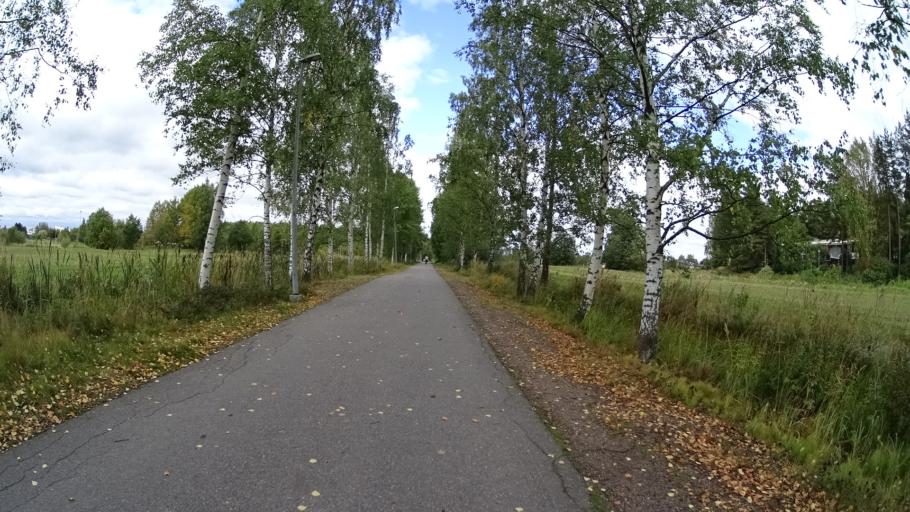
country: FI
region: Uusimaa
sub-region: Helsinki
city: Vantaa
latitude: 60.2455
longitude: 25.0258
